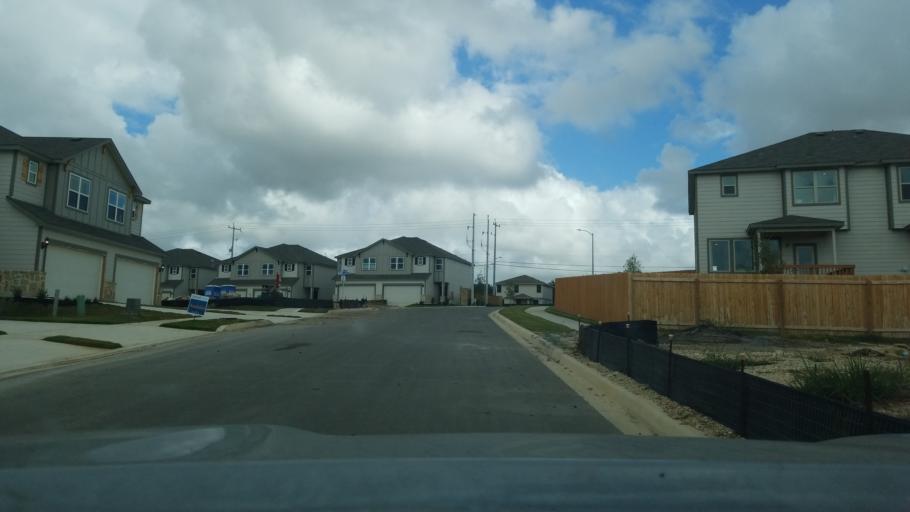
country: US
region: Texas
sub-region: Bexar County
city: Converse
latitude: 29.5325
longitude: -98.3139
